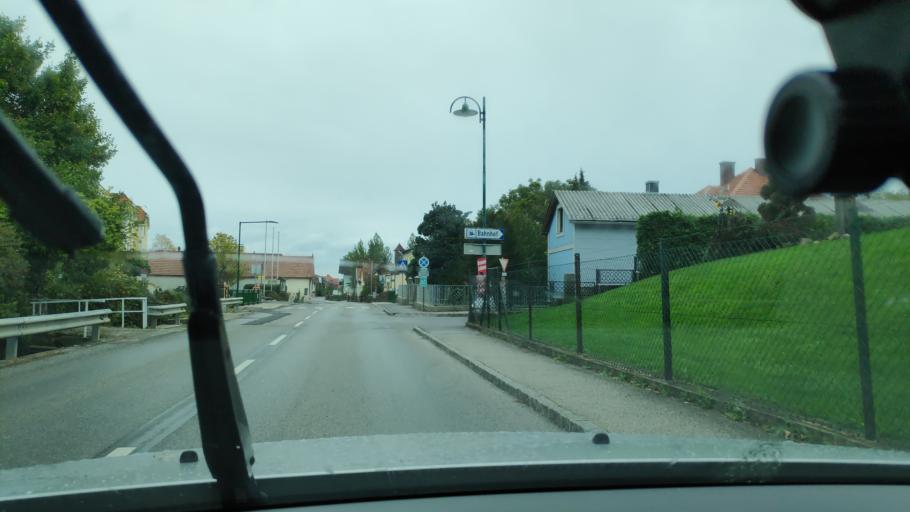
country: AT
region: Lower Austria
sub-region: Politischer Bezirk Neunkirchen
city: Willendorf am Steinfelde
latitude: 47.7904
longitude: 16.0518
